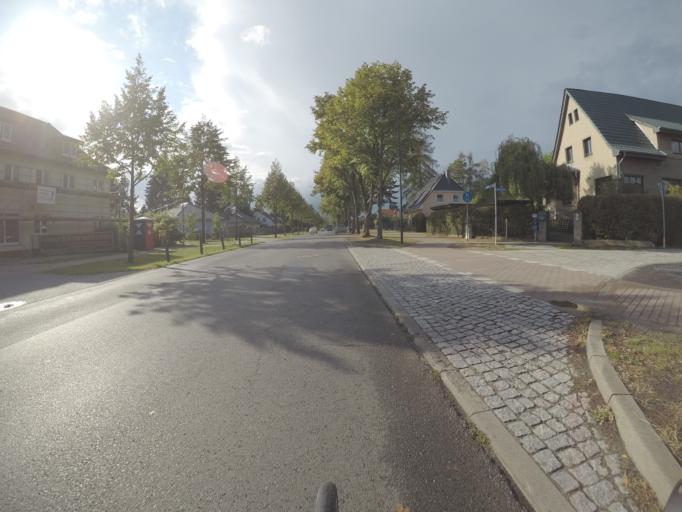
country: DE
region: Brandenburg
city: Petershagen
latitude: 52.5152
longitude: 13.7391
